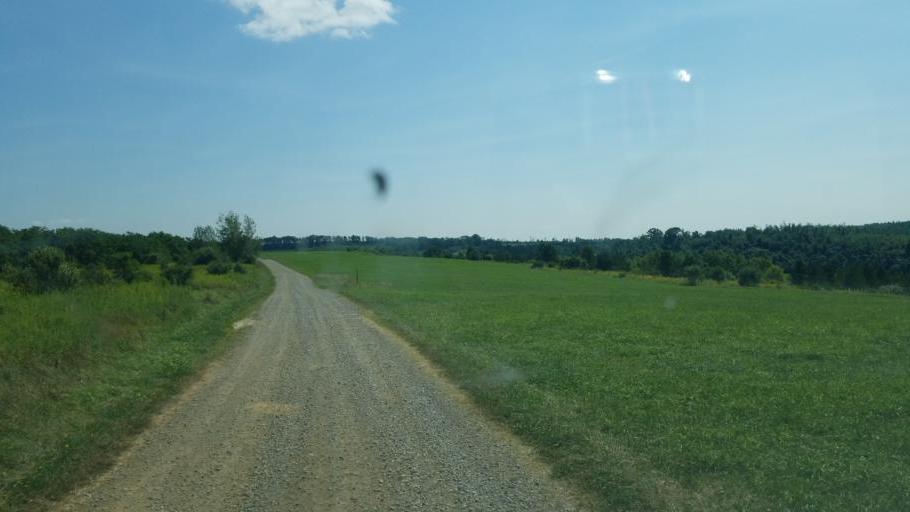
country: US
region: Pennsylvania
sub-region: Clarion County
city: Knox
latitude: 41.1080
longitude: -79.5331
